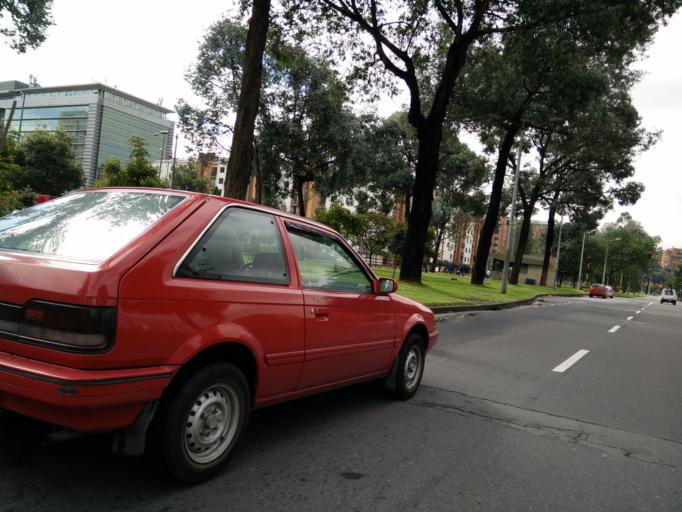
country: CO
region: Bogota D.C.
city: Bogota
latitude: 4.6566
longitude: -74.1086
